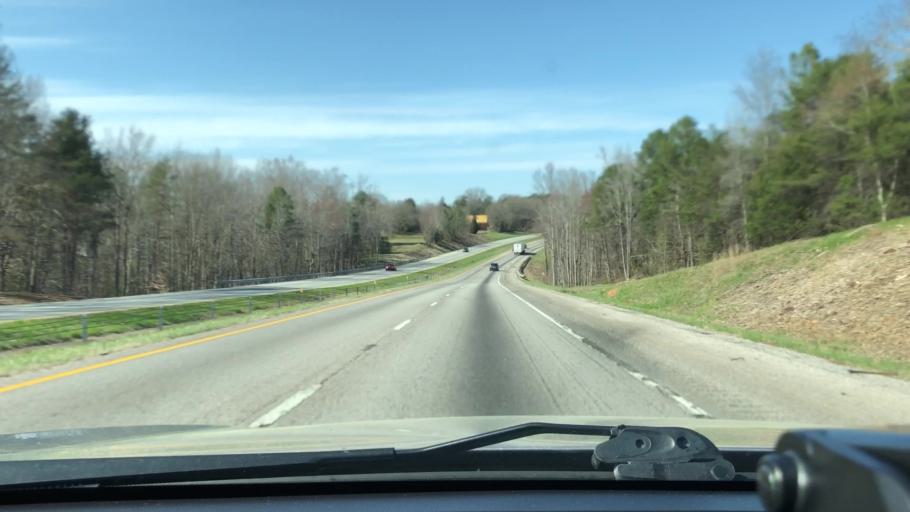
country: US
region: South Carolina
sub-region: Spartanburg County
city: Roebuck
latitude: 34.8825
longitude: -81.9924
